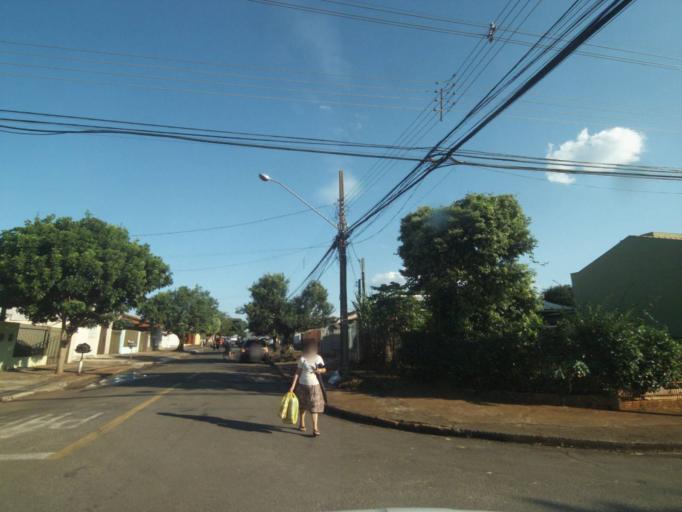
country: BR
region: Parana
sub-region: Londrina
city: Londrina
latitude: -23.3091
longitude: -51.2206
